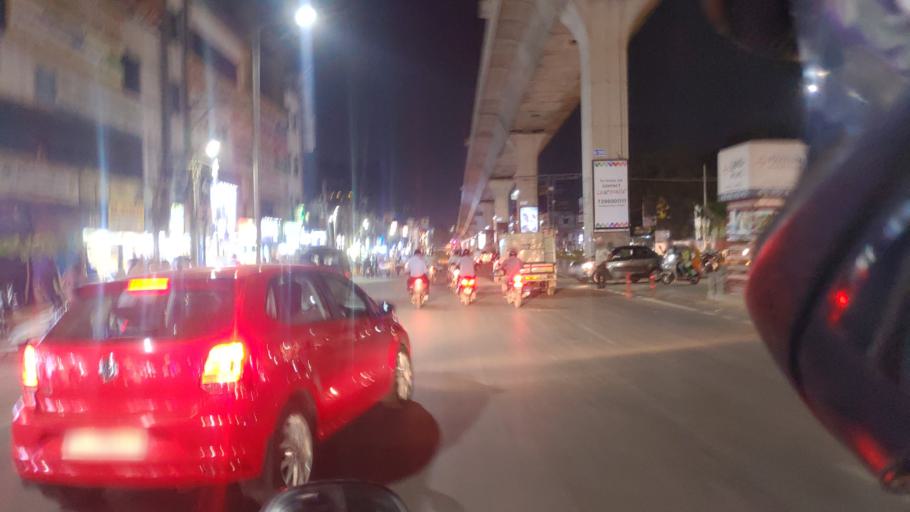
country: IN
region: Telangana
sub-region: Rangareddi
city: Gaddi Annaram
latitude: 17.3686
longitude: 78.5271
